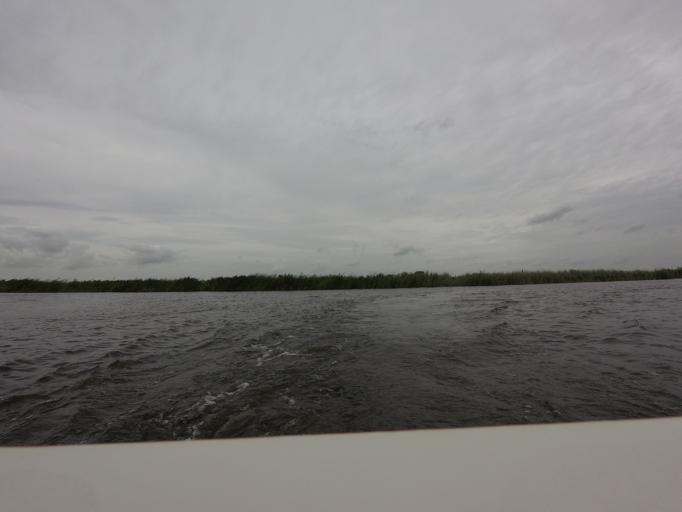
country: NL
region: Friesland
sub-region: Gemeente Boarnsterhim
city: Warten
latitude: 53.1171
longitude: 5.8862
